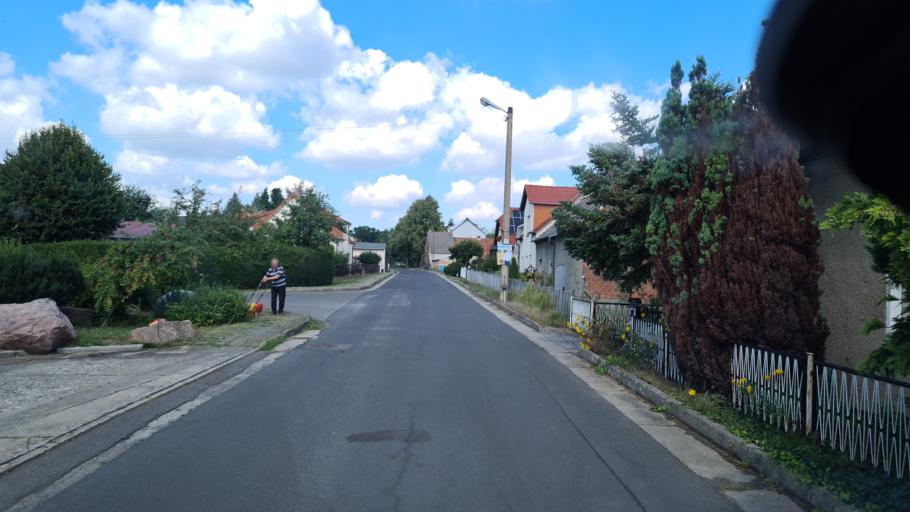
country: DE
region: Brandenburg
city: Spremberg
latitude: 51.6516
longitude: 14.3331
